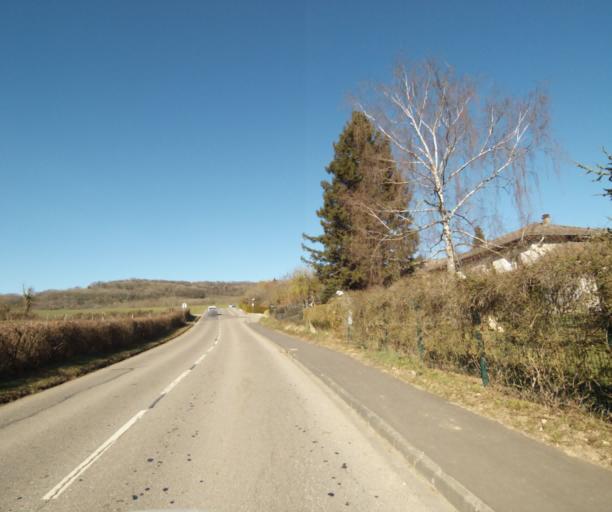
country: FR
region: Lorraine
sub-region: Departement de Meurthe-et-Moselle
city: Ludres
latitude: 48.6135
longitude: 6.1605
